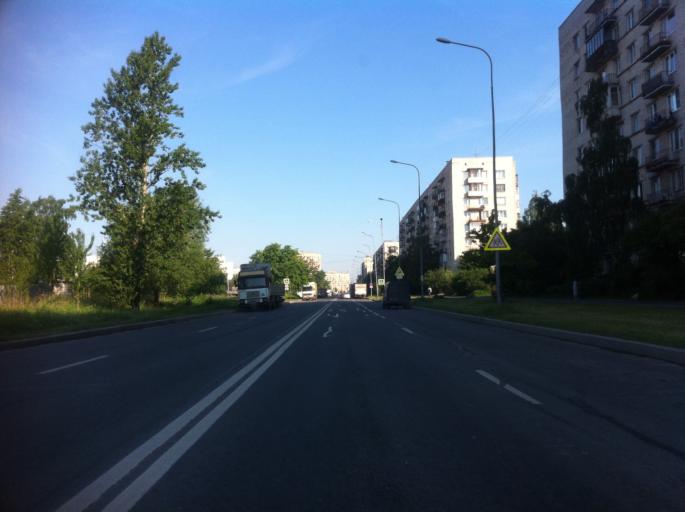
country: RU
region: St.-Petersburg
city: Dachnoye
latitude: 59.8356
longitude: 30.2460
